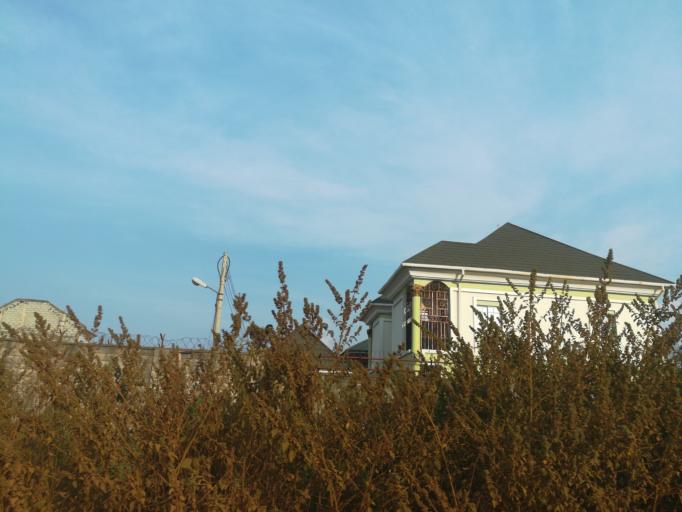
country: NG
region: Abuja Federal Capital Territory
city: Abuja
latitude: 9.0994
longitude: 7.3700
